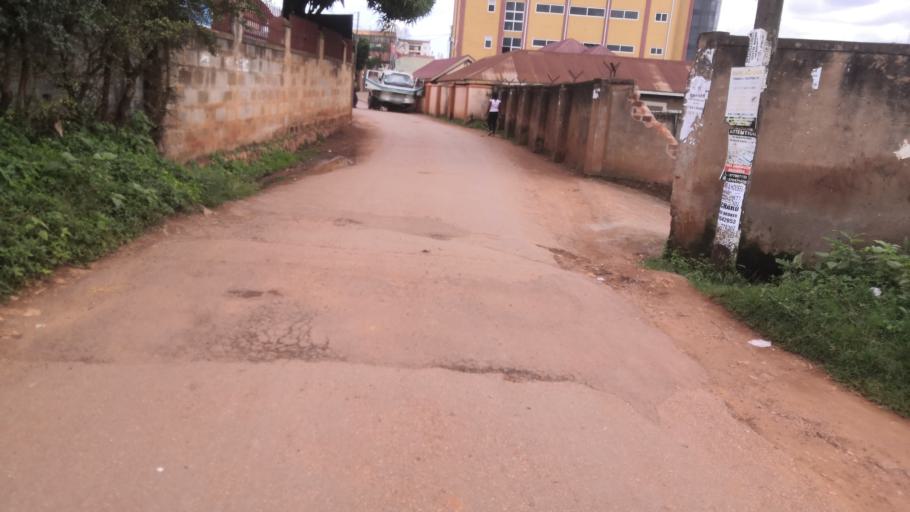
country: UG
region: Central Region
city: Kampala Central Division
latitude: 0.3301
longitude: 32.5624
